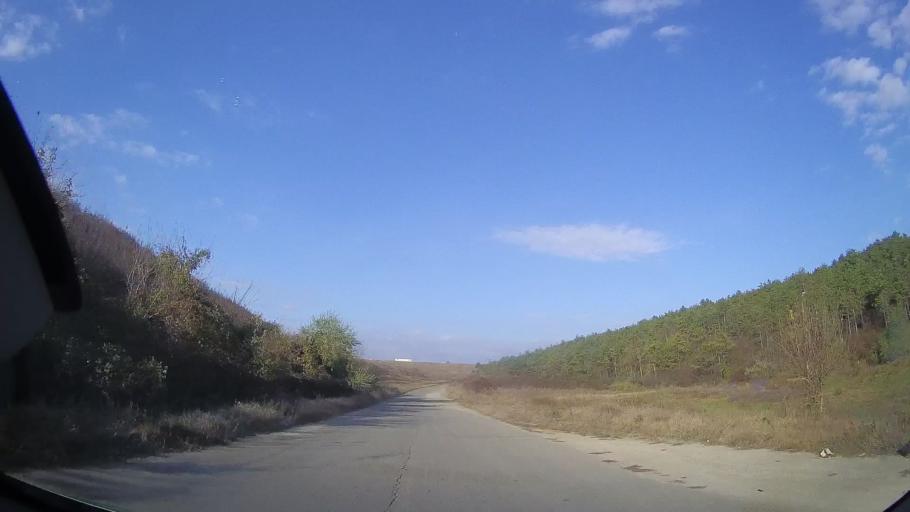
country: RO
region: Constanta
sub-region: Comuna Limanu
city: Limanu
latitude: 43.8156
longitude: 28.5175
